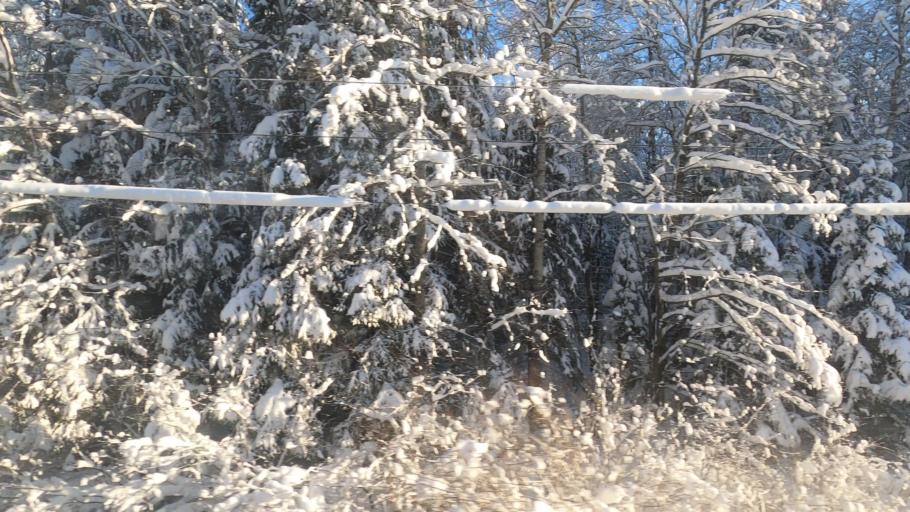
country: RU
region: Moskovskaya
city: Zhukovka
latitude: 56.4967
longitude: 37.5521
